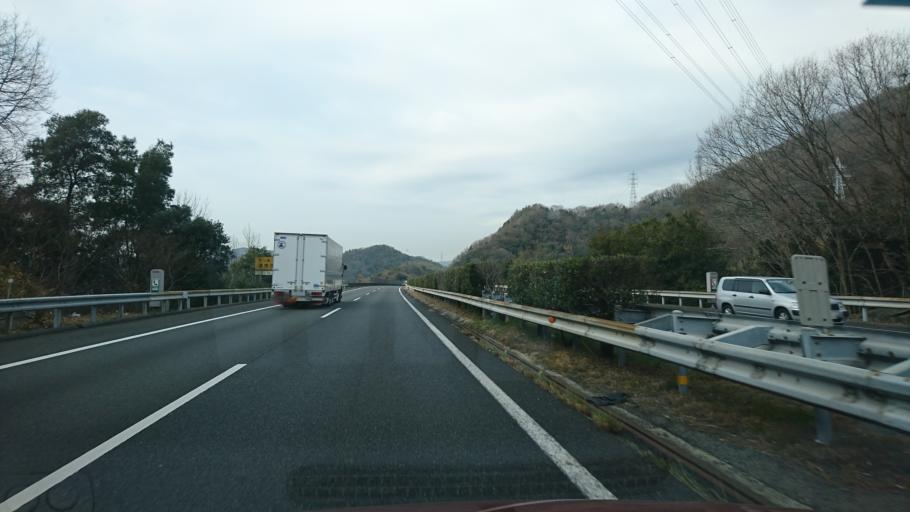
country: JP
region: Okayama
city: Kasaoka
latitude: 34.5317
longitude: 133.5384
